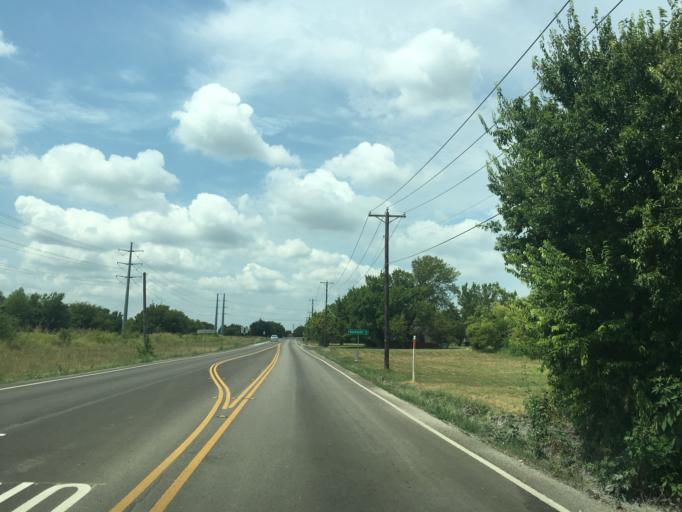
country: US
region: Texas
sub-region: Rockwall County
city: Fate
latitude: 32.9410
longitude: -96.3842
